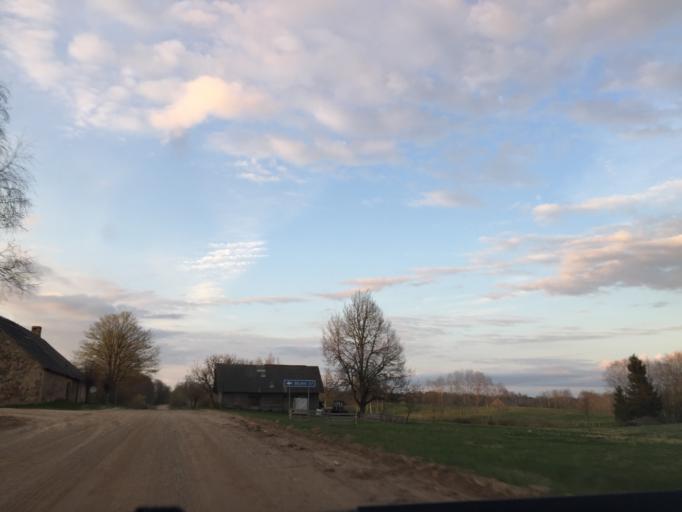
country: LV
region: Gulbenes Rajons
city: Gulbene
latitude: 57.2383
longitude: 26.8157
